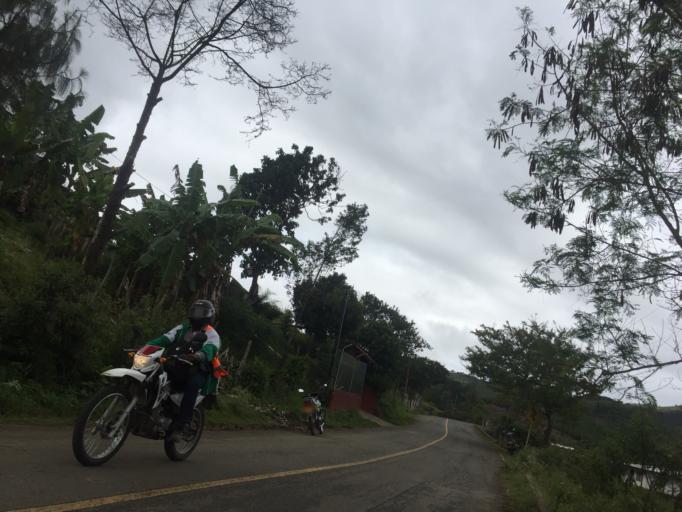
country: CO
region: Valle del Cauca
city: Dagua
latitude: 3.6921
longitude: -76.5915
